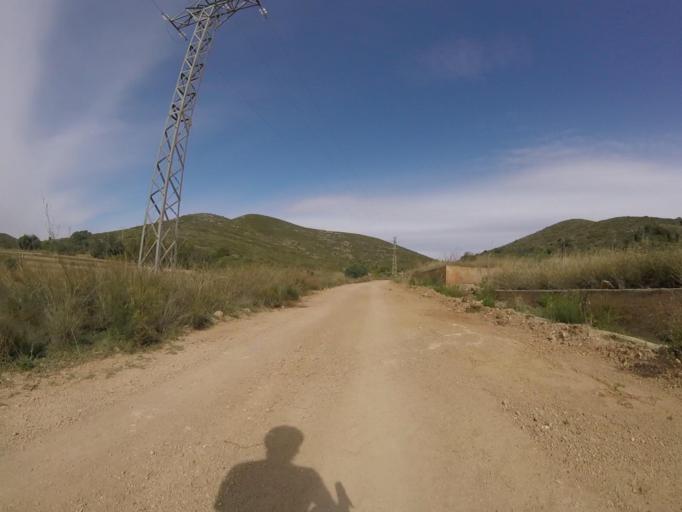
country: ES
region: Valencia
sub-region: Provincia de Castello
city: Torreblanca
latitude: 40.1966
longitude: 0.1580
